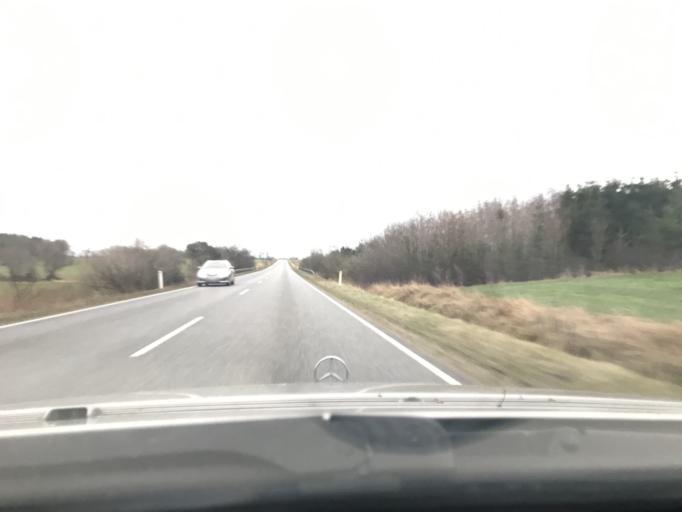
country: DK
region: South Denmark
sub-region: Tonder Kommune
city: Toftlund
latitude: 55.1179
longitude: 9.1599
